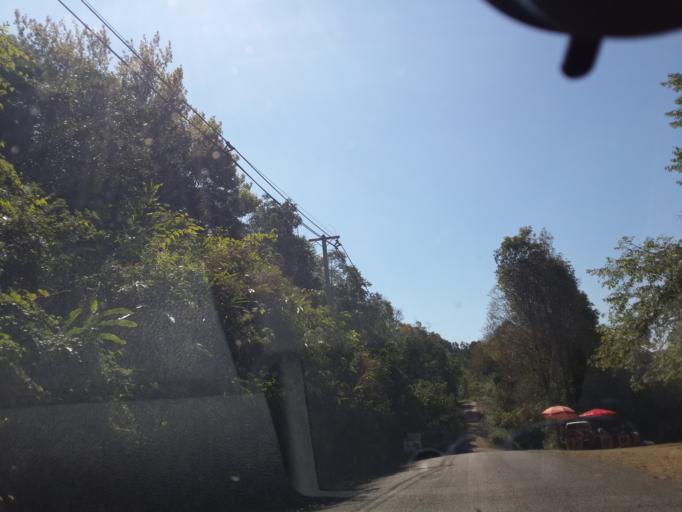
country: TH
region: Chiang Mai
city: Fang
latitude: 19.9032
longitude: 99.0518
